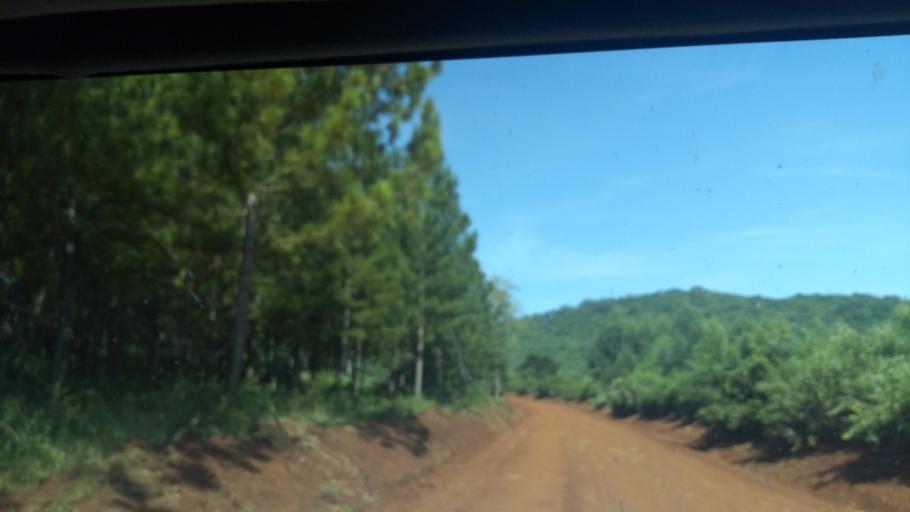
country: UG
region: Western Region
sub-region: Masindi District
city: Masindi
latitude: 1.6503
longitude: 31.7792
